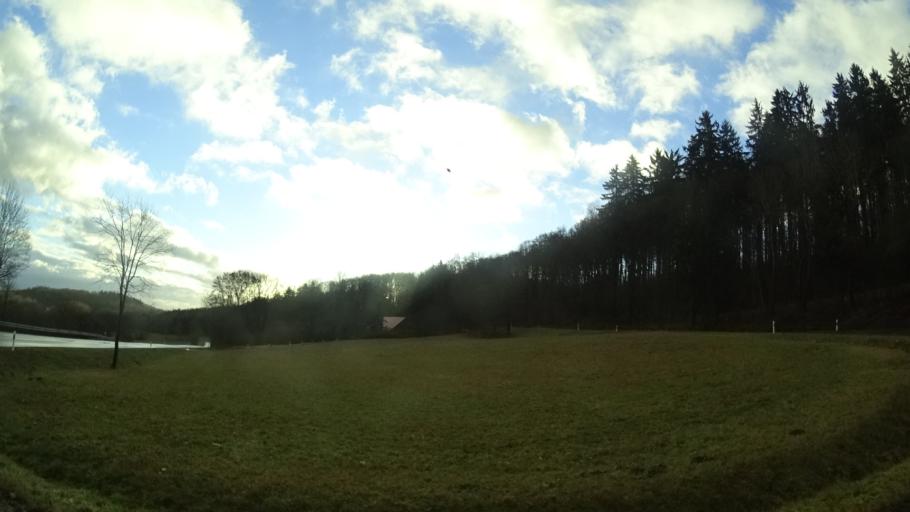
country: DE
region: Bavaria
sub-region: Regierungsbezirk Unterfranken
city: Hausen
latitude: 50.4865
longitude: 10.0979
